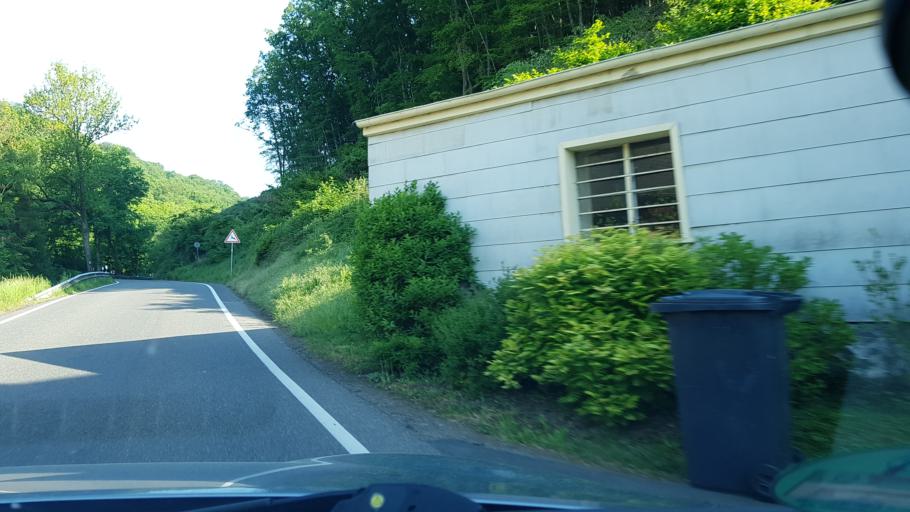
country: DE
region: Rheinland-Pfalz
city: Kadenbach
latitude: 50.3739
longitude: 7.7393
